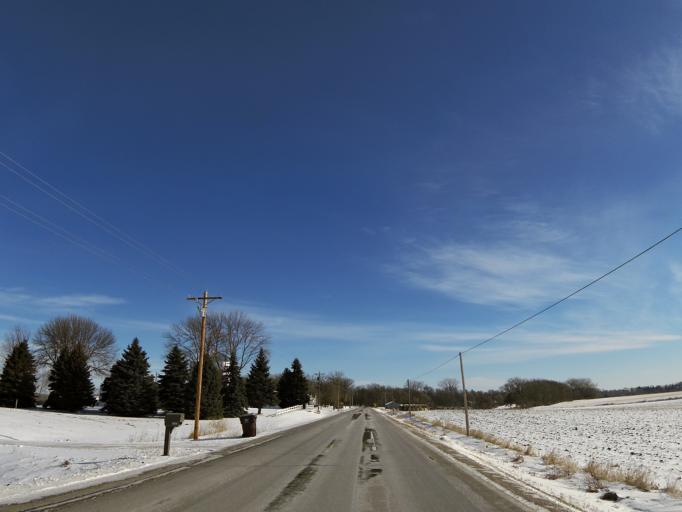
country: US
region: Minnesota
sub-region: Washington County
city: Cottage Grove
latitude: 44.7445
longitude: -92.9423
